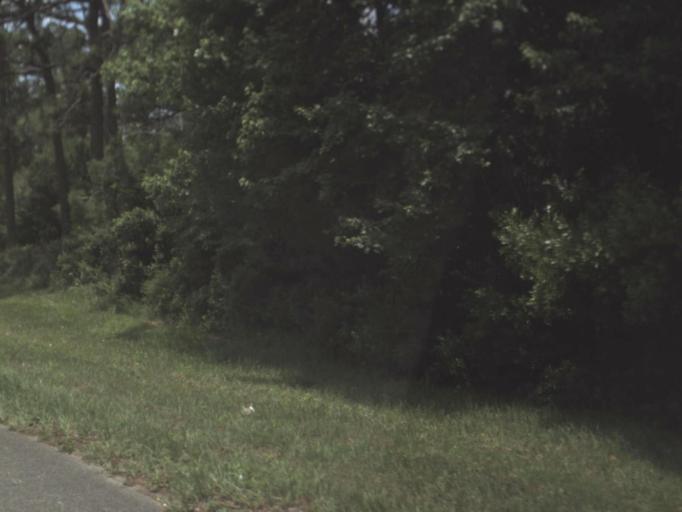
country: US
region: Florida
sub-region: Nassau County
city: Yulee
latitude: 30.6670
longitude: -81.6380
